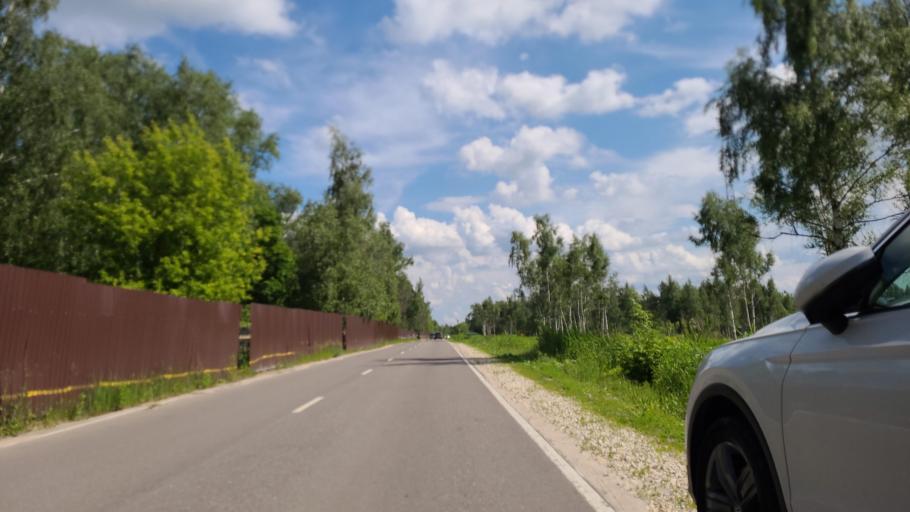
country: RU
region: Moskovskaya
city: Konobeyevo
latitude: 55.4009
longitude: 38.6767
